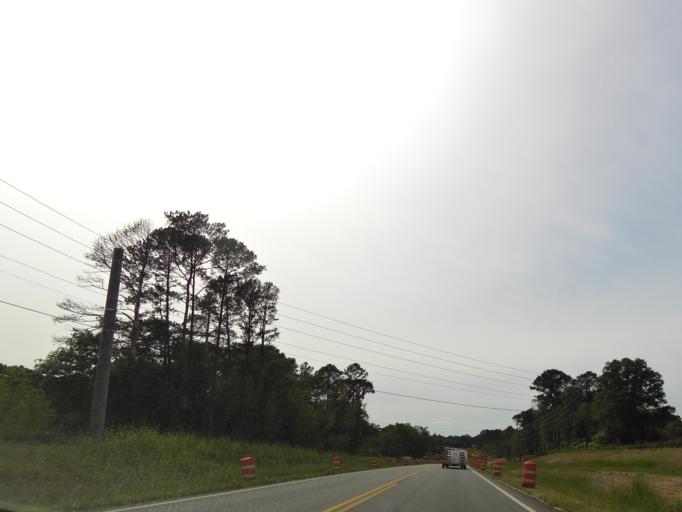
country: US
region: Georgia
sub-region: Houston County
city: Robins Air Force Base
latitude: 32.5507
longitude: -83.6077
